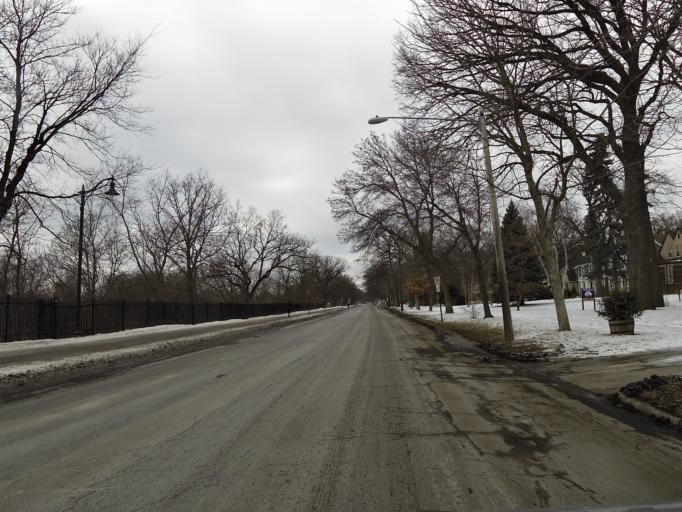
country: US
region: Minnesota
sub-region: Ramsey County
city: Lauderdale
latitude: 44.9612
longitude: -93.2157
